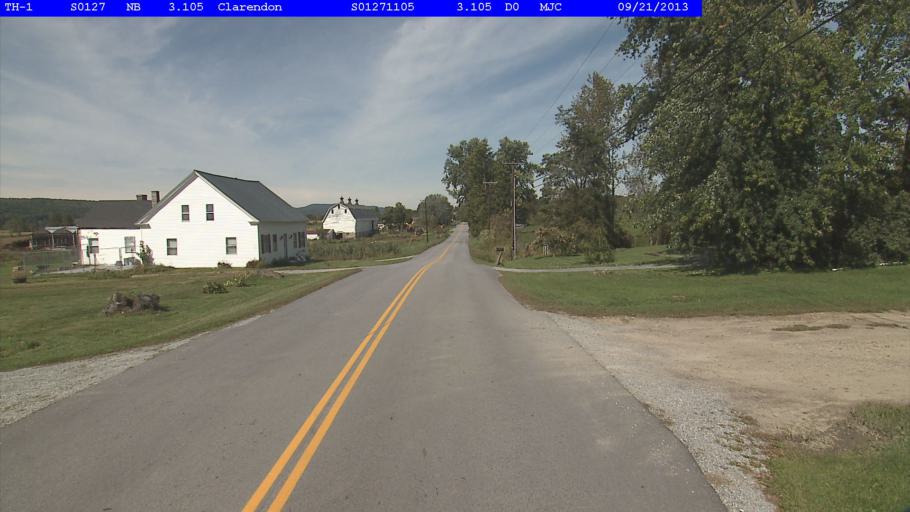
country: US
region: Vermont
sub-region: Rutland County
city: Rutland
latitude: 43.5581
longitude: -72.9717
